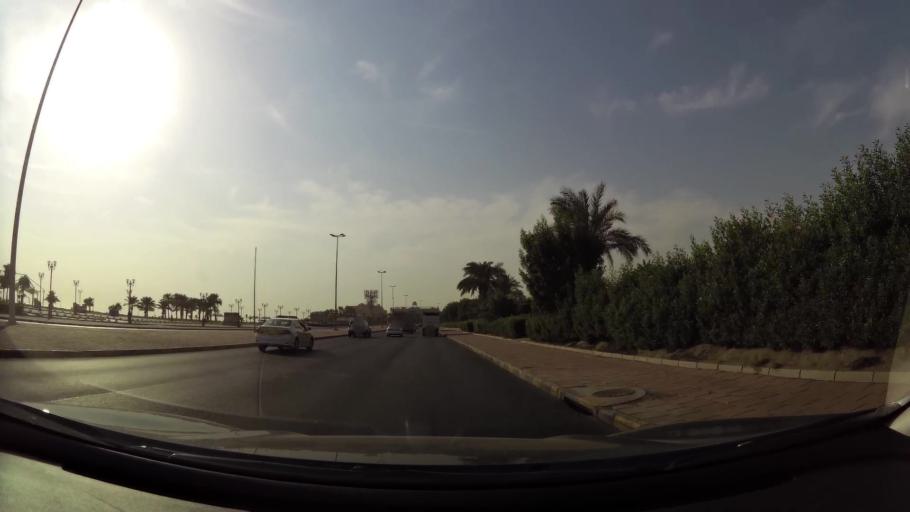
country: KW
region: Muhafazat Hawalli
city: Salwa
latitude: 29.2770
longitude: 48.0884
